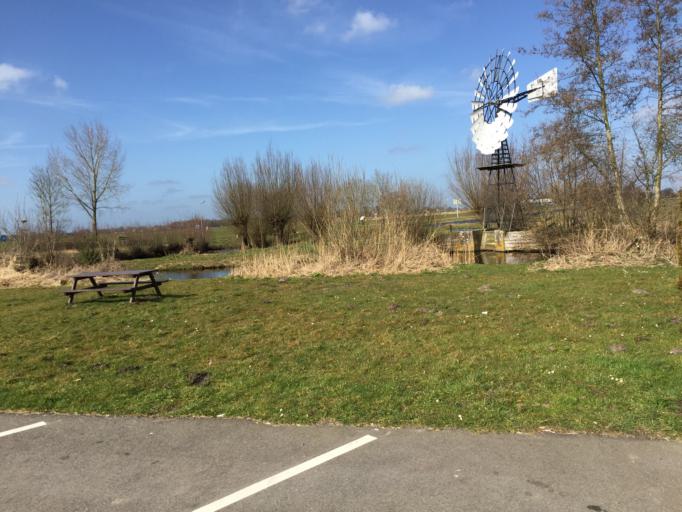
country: NL
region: South Holland
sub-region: Molenwaard
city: Nieuw-Lekkerland
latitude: 51.9293
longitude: 4.7175
